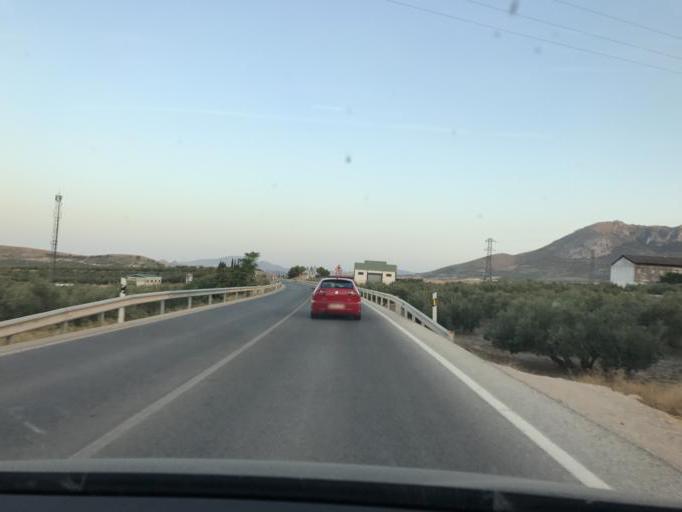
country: ES
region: Andalusia
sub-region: Provincia de Jaen
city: Jodar
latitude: 37.8512
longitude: -3.3500
